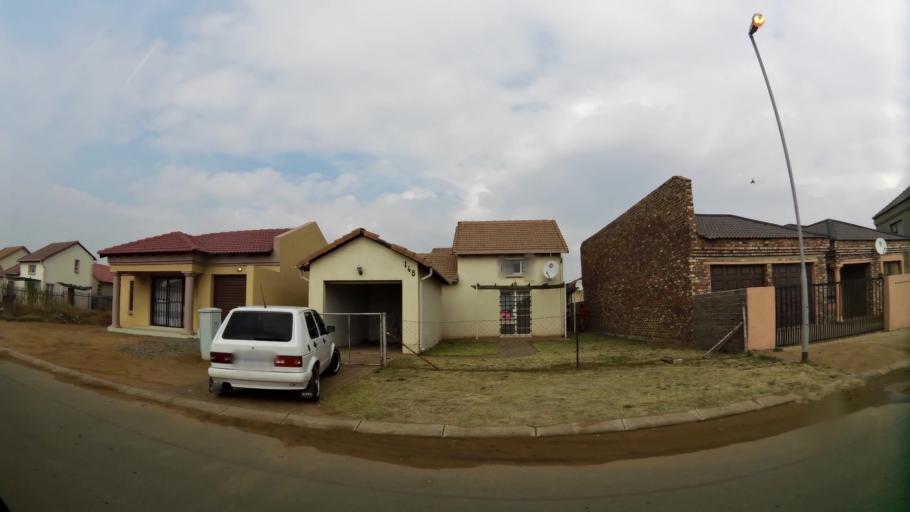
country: ZA
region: Gauteng
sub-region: Sedibeng District Municipality
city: Vanderbijlpark
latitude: -26.6845
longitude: 27.8508
